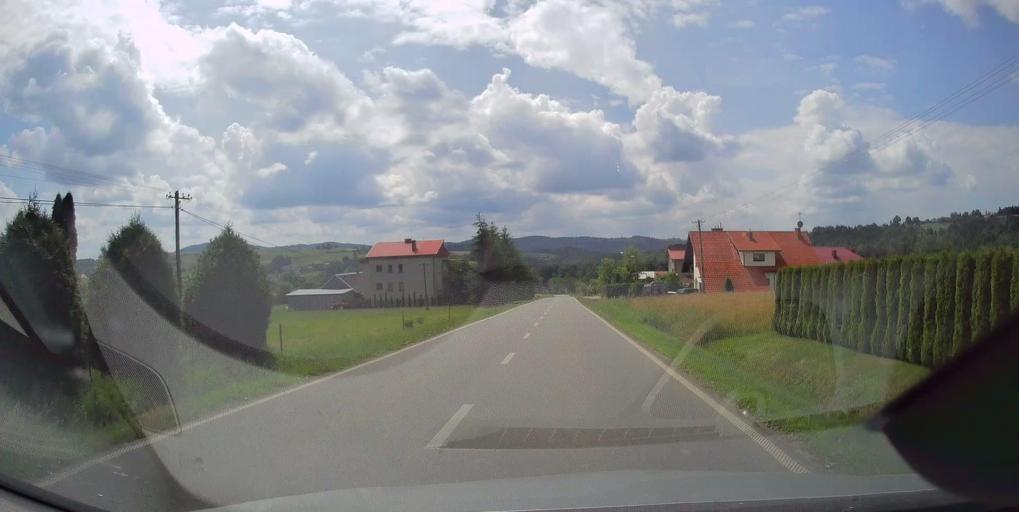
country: PL
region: Lesser Poland Voivodeship
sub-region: Powiat nowosadecki
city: Korzenna
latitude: 49.6815
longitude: 20.7760
